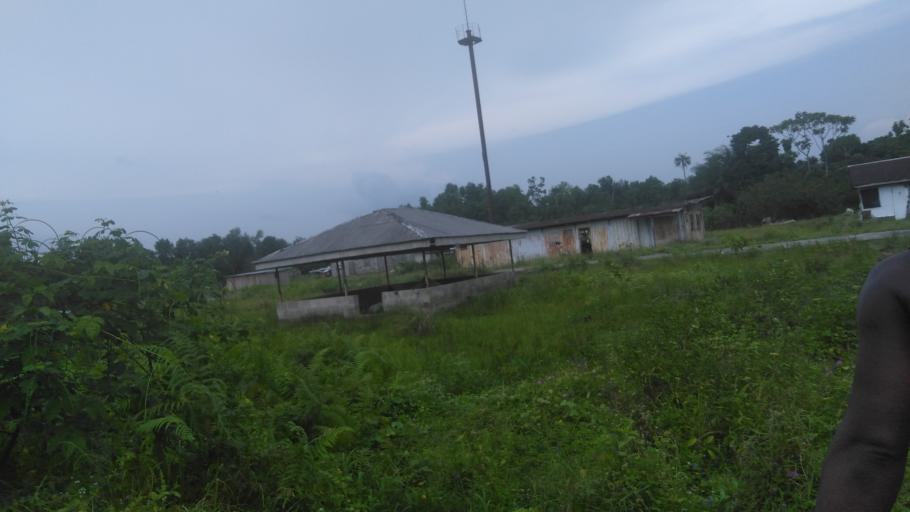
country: NG
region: Delta
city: Sapele
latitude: 5.8418
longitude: 5.1268
